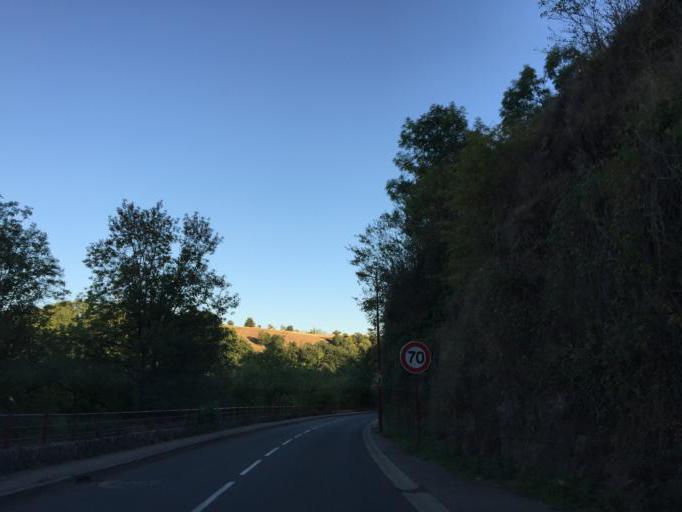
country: FR
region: Midi-Pyrenees
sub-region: Departement de l'Aveyron
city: Rodez
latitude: 44.3519
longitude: 2.5800
